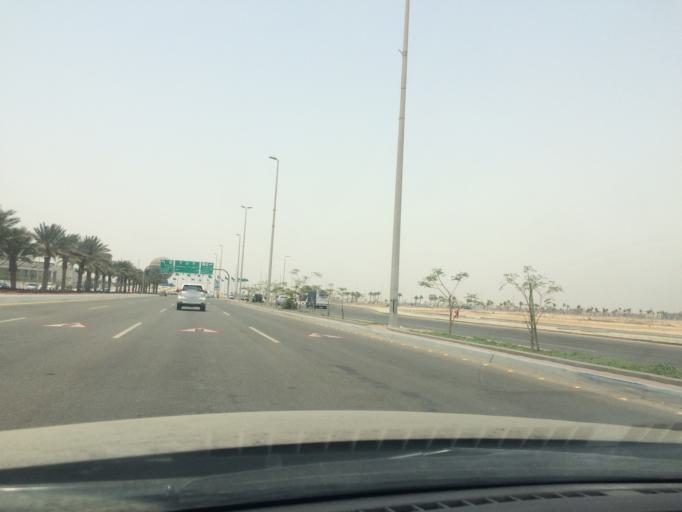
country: SA
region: Makkah
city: Jeddah
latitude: 21.6611
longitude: 39.1111
